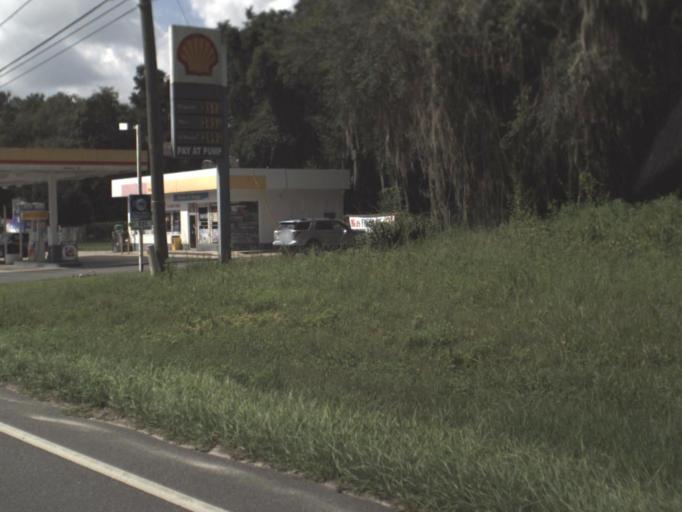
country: US
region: Florida
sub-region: Citrus County
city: Hernando
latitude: 28.8965
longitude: -82.3720
